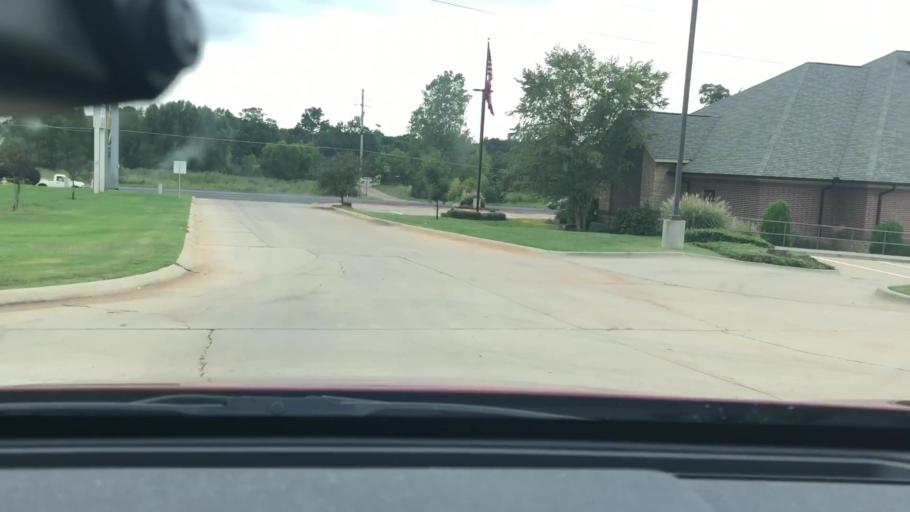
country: US
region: Arkansas
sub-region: Miller County
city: Texarkana
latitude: 33.4314
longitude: -94.0006
